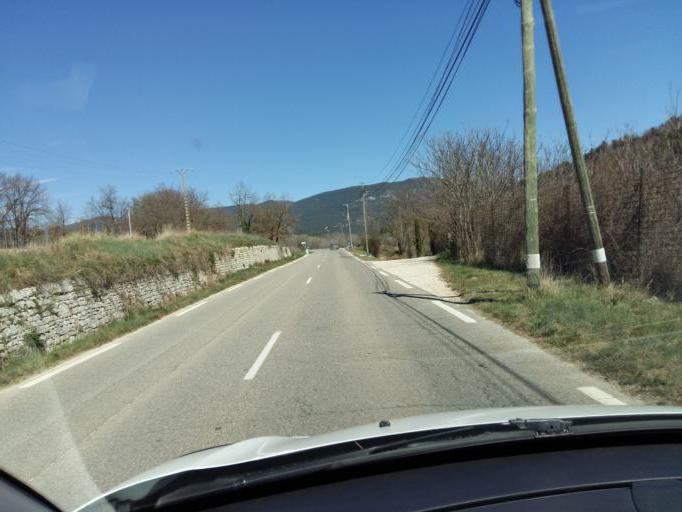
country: FR
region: Provence-Alpes-Cote d'Azur
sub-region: Departement du Vaucluse
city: Apt
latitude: 43.8981
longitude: 5.4327
